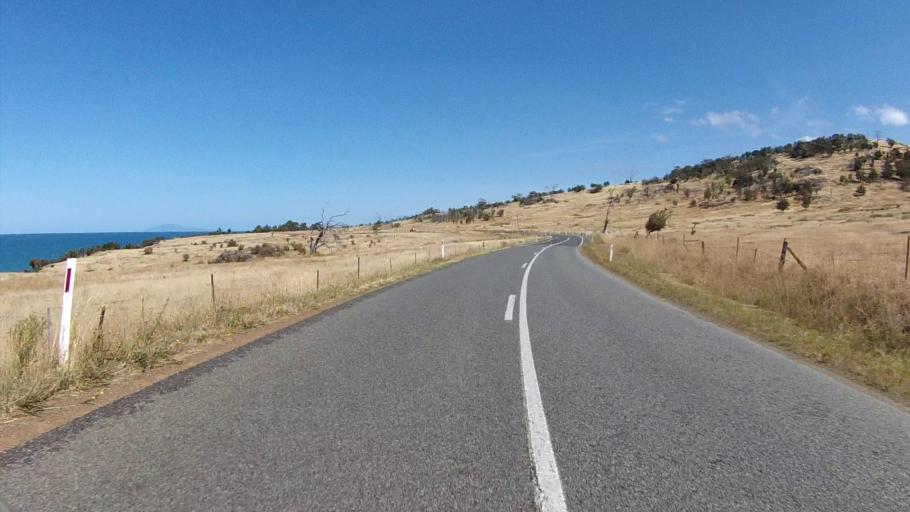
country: AU
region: Tasmania
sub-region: Sorell
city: Sorell
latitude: -42.1777
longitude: 148.0681
